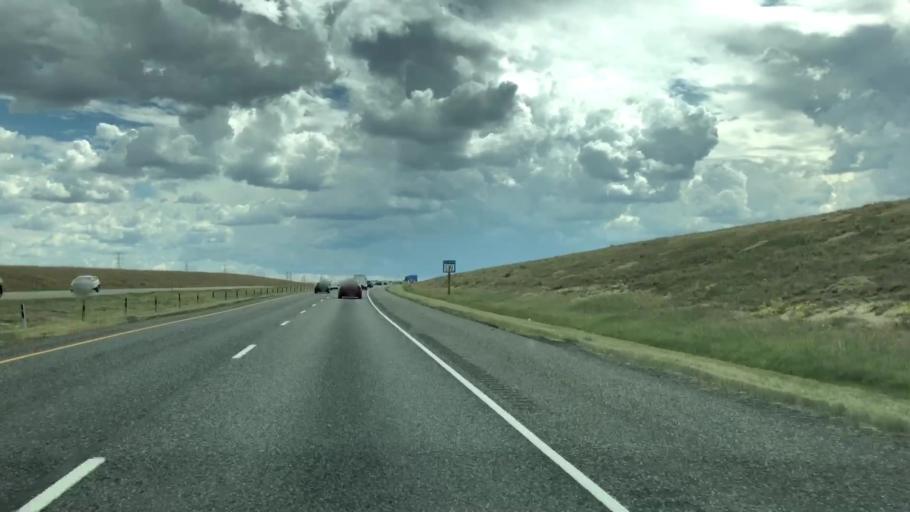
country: US
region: Colorado
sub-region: Arapahoe County
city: Dove Valley
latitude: 39.6511
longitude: -104.7195
